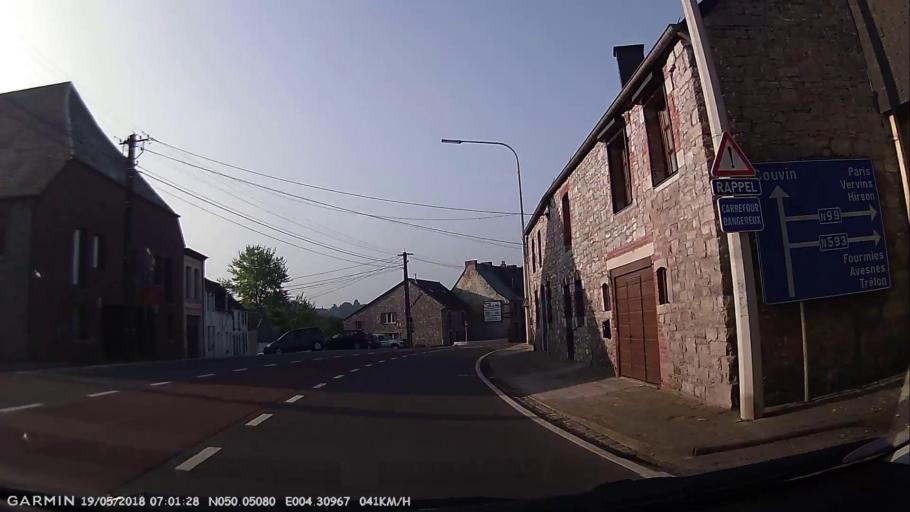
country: BE
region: Wallonia
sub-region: Province du Hainaut
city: Chimay
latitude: 50.0508
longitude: 4.3099
